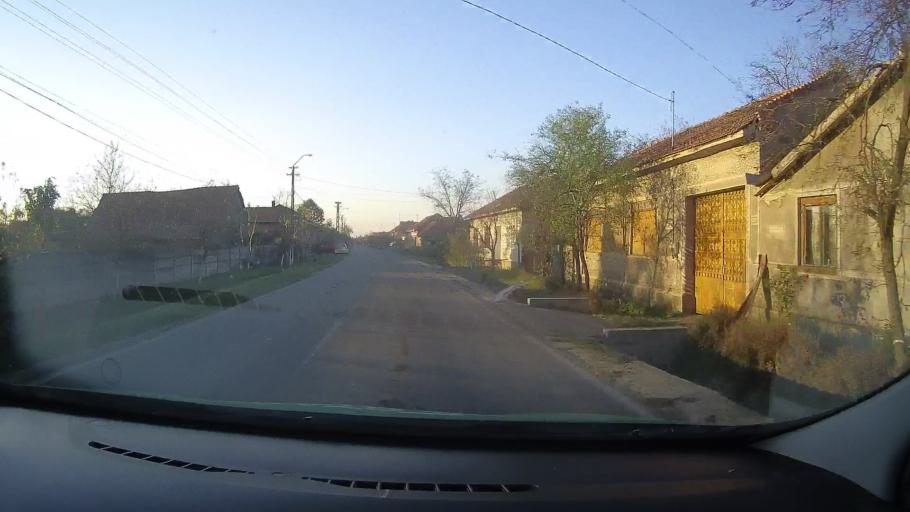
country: RO
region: Timis
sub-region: Comuna Traian Vuia
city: Traian Vuia
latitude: 45.7928
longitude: 22.0720
